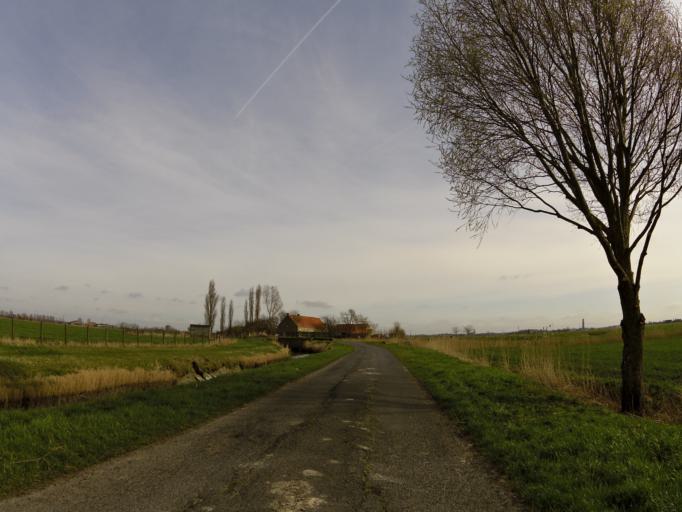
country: BE
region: Flanders
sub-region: Provincie West-Vlaanderen
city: Diksmuide
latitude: 51.0600
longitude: 2.8290
